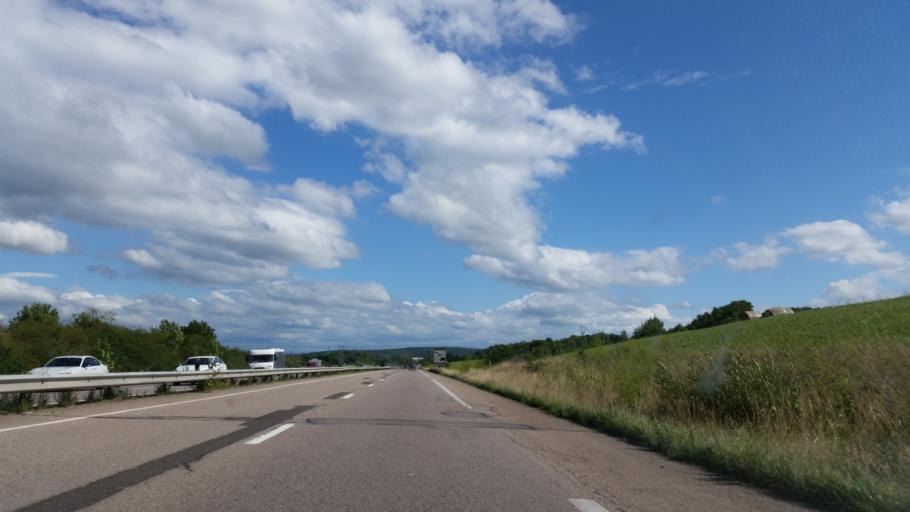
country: FR
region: Lorraine
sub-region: Departement des Vosges
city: Charmes
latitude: 48.3527
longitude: 6.3004
